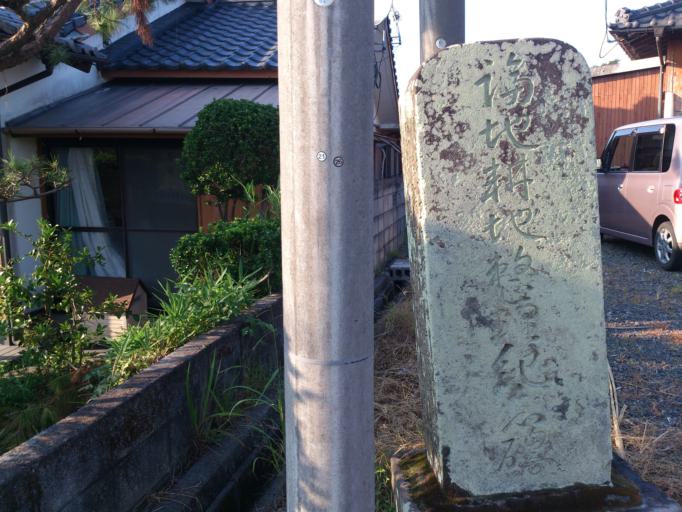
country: JP
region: Kagoshima
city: Kanoya
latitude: 31.3440
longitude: 130.9163
